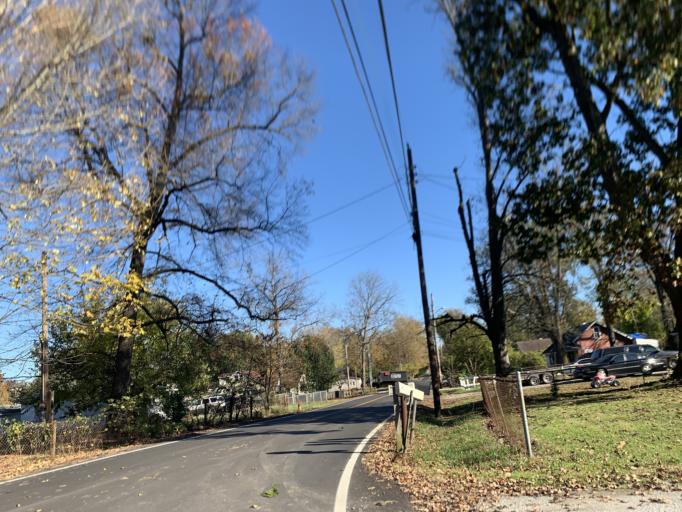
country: US
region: Kentucky
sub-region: Jefferson County
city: Pleasure Ridge Park
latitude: 38.1576
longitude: -85.8757
